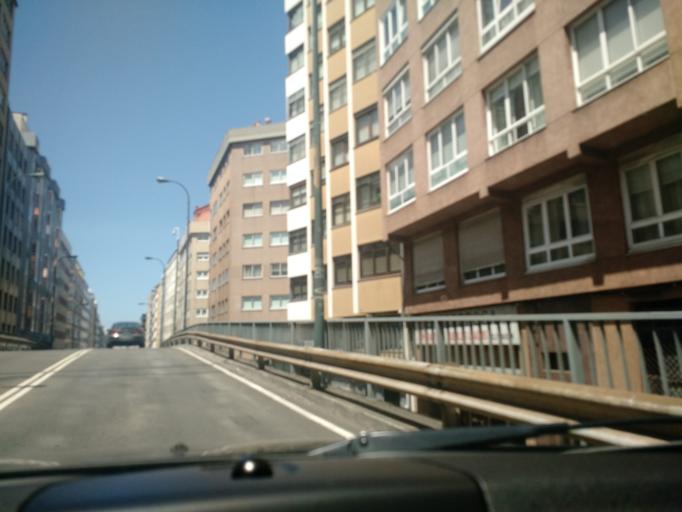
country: ES
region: Galicia
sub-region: Provincia da Coruna
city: A Coruna
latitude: 43.3609
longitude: -8.4154
